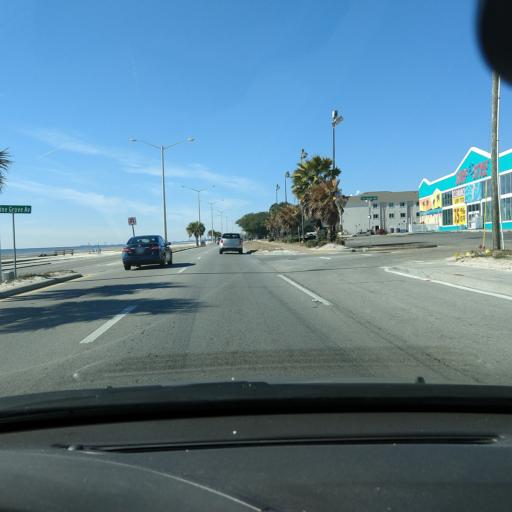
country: US
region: Mississippi
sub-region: Harrison County
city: Biloxi
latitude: 30.3903
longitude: -88.9801
